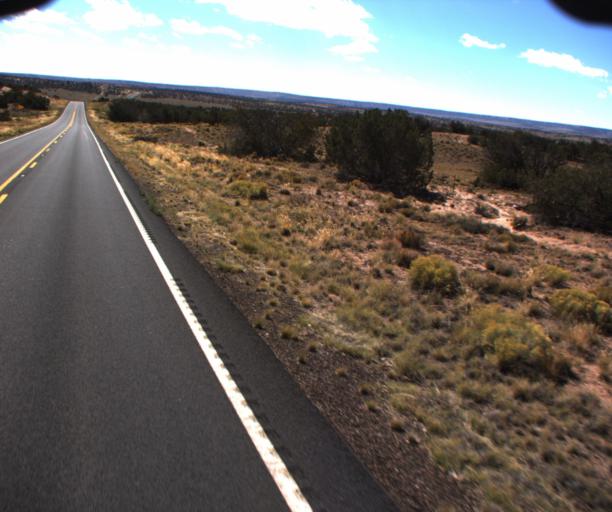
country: US
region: Arizona
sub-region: Apache County
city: Houck
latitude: 35.1064
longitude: -109.3163
